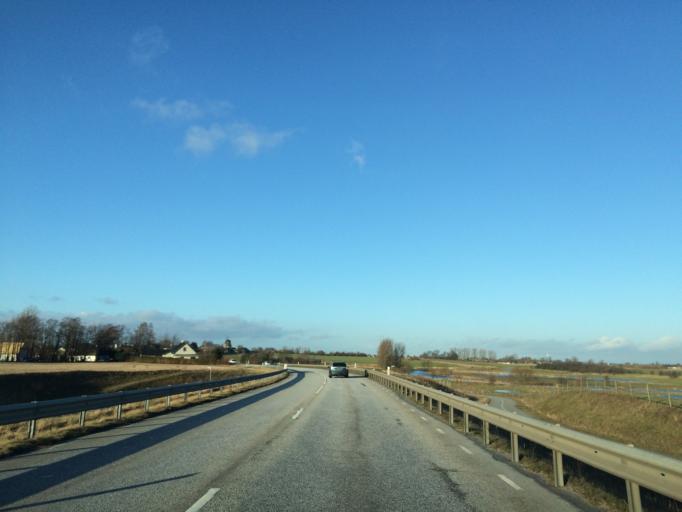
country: SE
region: Skane
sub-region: Kavlinge Kommun
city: Loddekopinge
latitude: 55.7504
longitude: 13.0273
